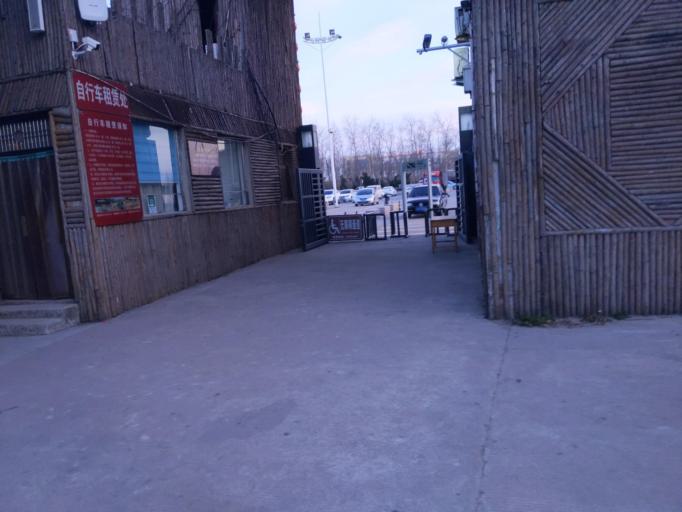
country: CN
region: Henan Sheng
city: Puyang
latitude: 35.7763
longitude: 114.9464
